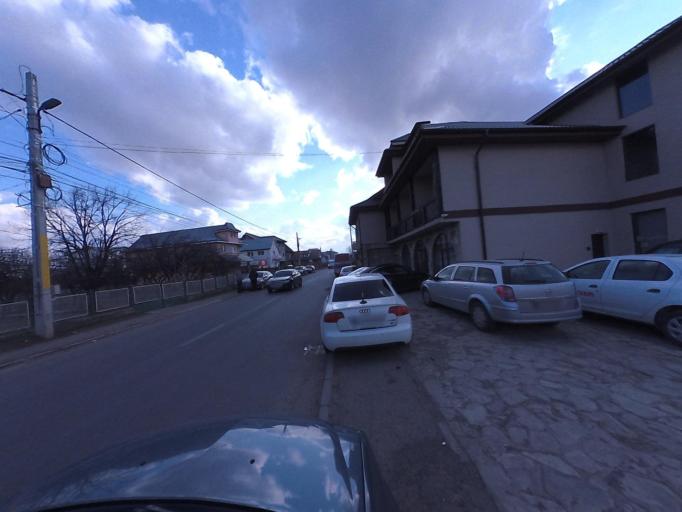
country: RO
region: Neamt
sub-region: Oras Targu Neamt
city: Targu Neamt
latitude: 47.2044
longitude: 26.3732
